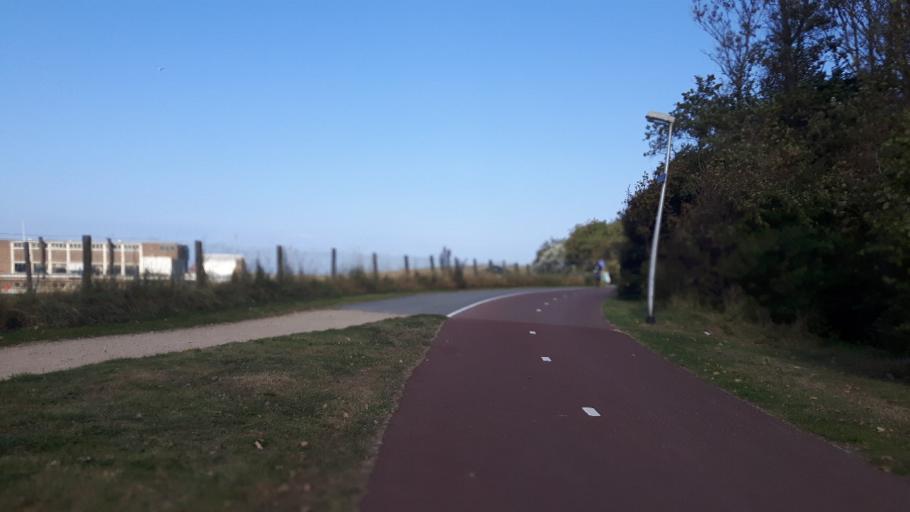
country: NL
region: South Holland
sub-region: Gemeente Katwijk
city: Katwijk aan Zee
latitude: 52.2072
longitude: 4.4094
